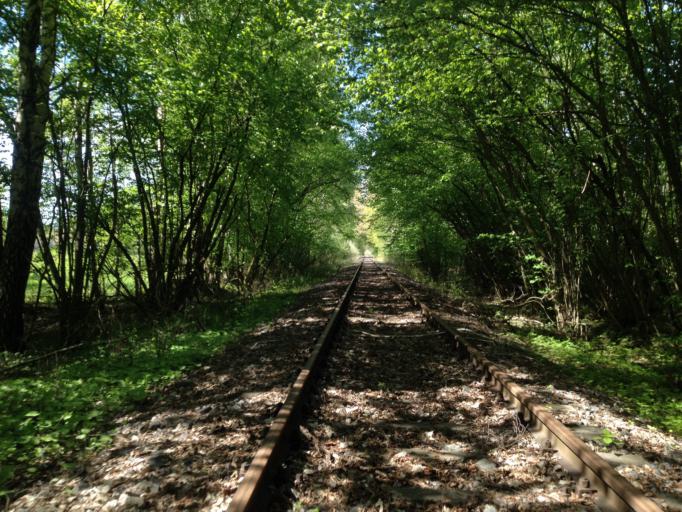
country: DE
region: Brandenburg
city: Templin
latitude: 53.1279
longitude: 13.4427
